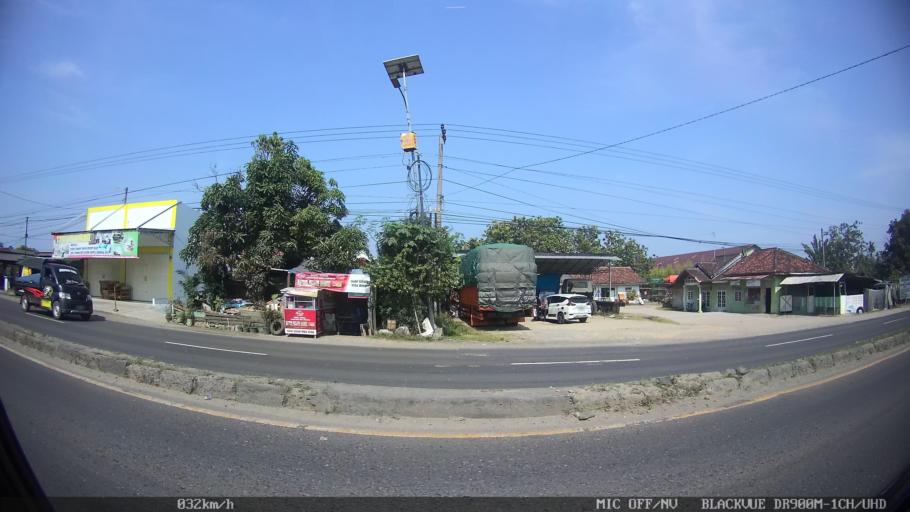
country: ID
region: Lampung
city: Natar
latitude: -5.2660
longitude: 105.1861
